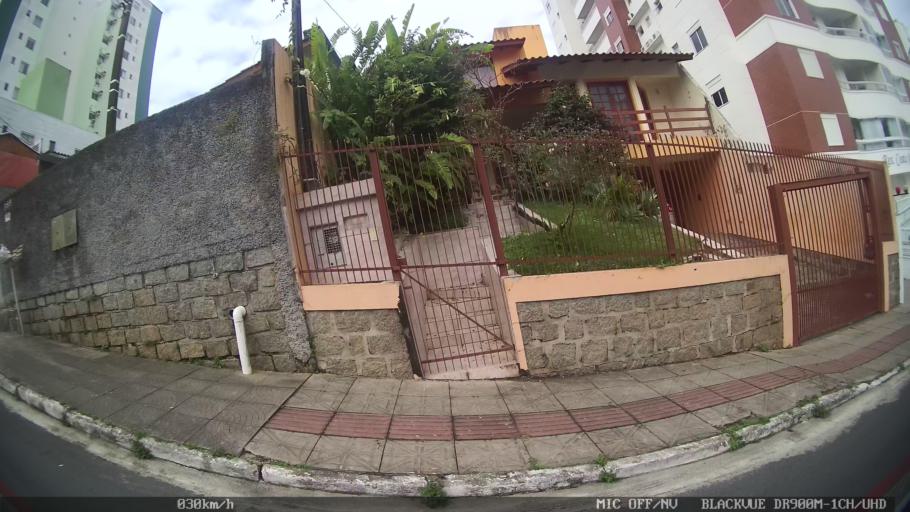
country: BR
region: Santa Catarina
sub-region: Sao Jose
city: Campinas
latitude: -27.5761
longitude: -48.6052
